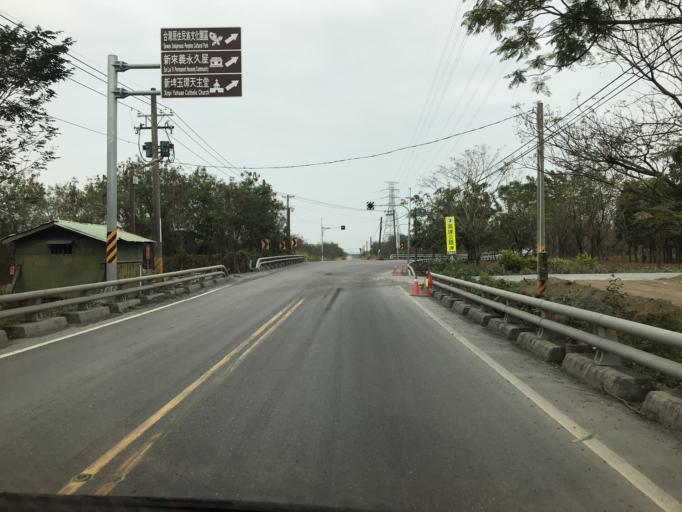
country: TW
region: Taiwan
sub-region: Pingtung
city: Pingtung
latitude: 22.4453
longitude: 120.6051
